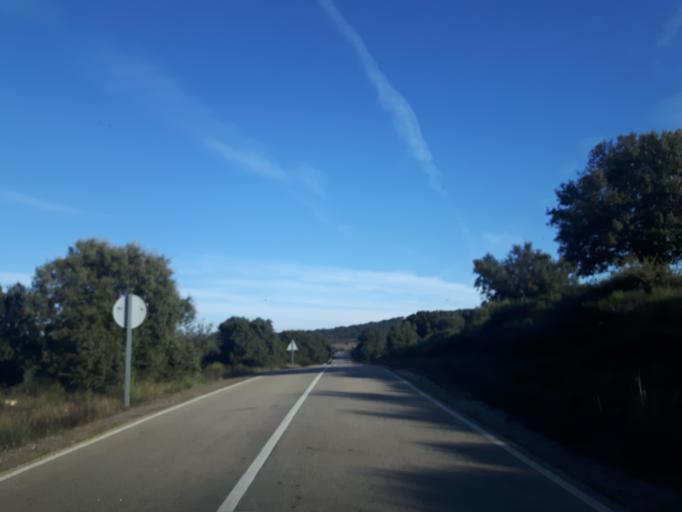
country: ES
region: Castille and Leon
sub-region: Provincia de Salamanca
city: Olmedo de Camaces
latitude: 40.8862
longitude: -6.6244
